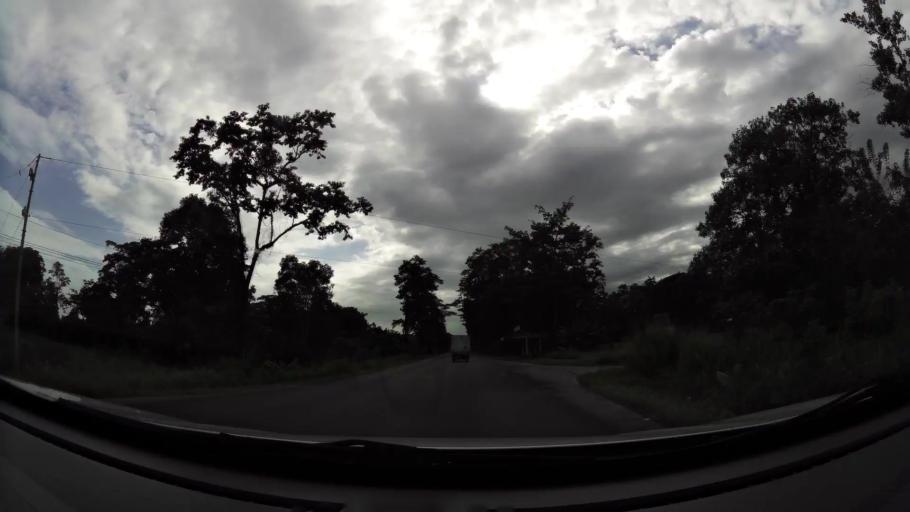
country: CR
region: Limon
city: Pocora
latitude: 10.1803
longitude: -83.6228
